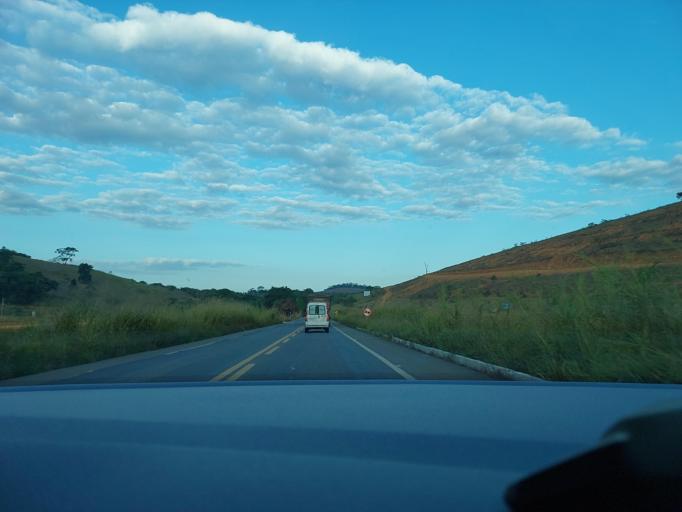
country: BR
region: Minas Gerais
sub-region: Muriae
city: Muriae
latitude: -21.1408
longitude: -42.1722
